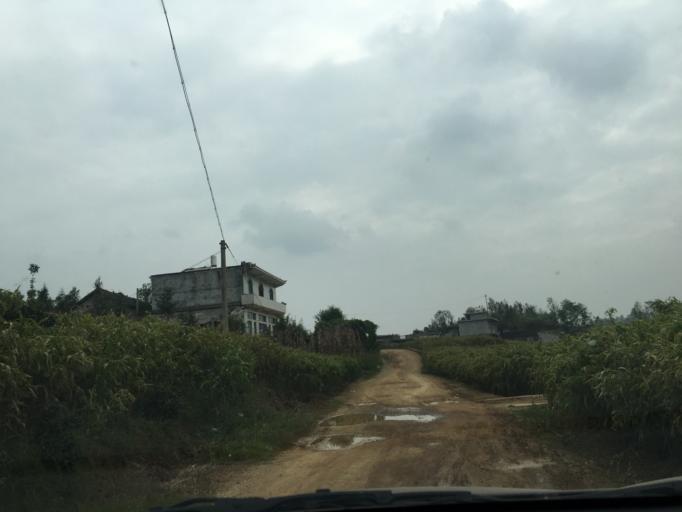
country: CN
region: Guangxi Zhuangzu Zizhiqu
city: Xinzhou
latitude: 25.5409
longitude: 105.5316
